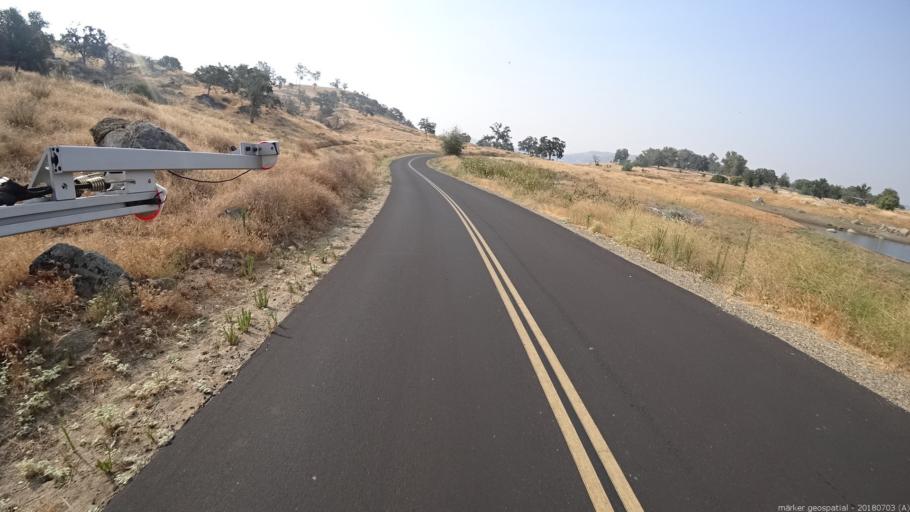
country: US
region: California
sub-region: Fresno County
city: Auberry
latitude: 37.0241
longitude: -119.6672
